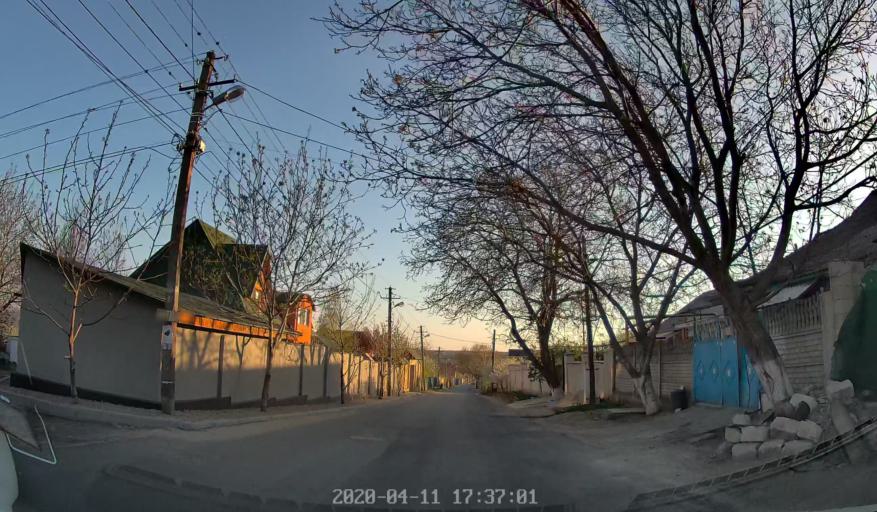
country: MD
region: Laloveni
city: Ialoveni
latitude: 46.9809
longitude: 28.8023
